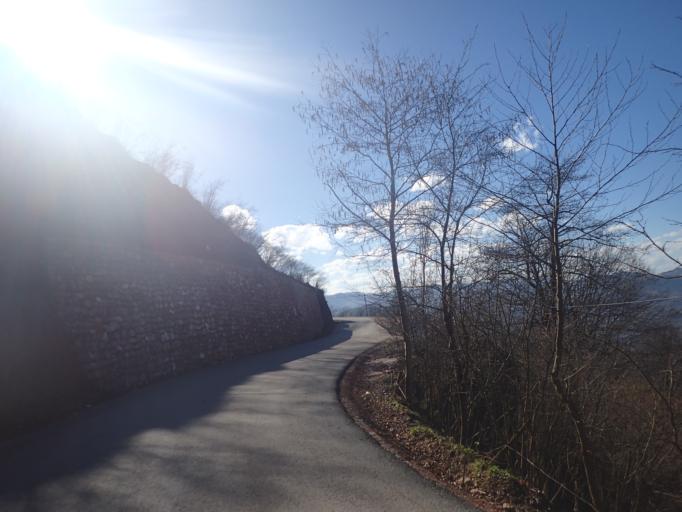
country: TR
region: Ordu
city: Camas
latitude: 40.8923
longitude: 37.5170
